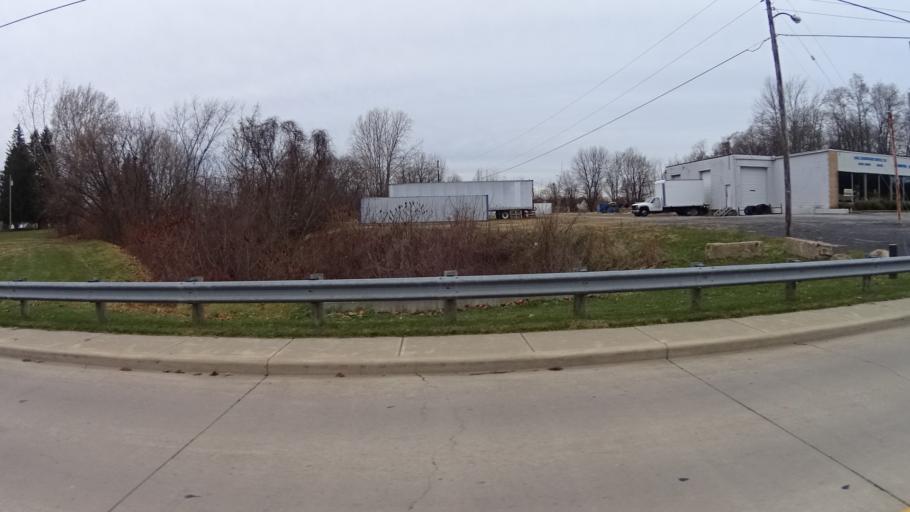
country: US
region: Ohio
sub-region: Lorain County
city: North Ridgeville
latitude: 41.3670
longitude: -81.9991
